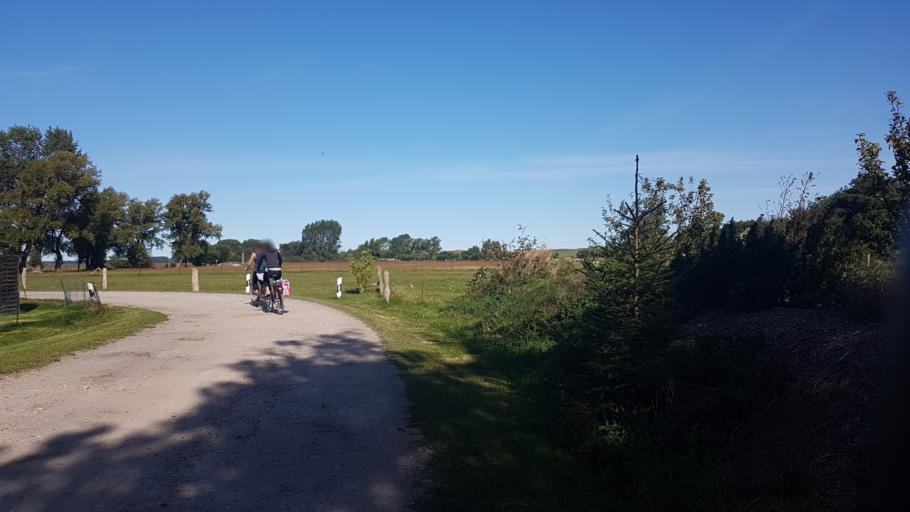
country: DE
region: Mecklenburg-Vorpommern
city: Sagard
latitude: 54.5267
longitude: 13.5161
